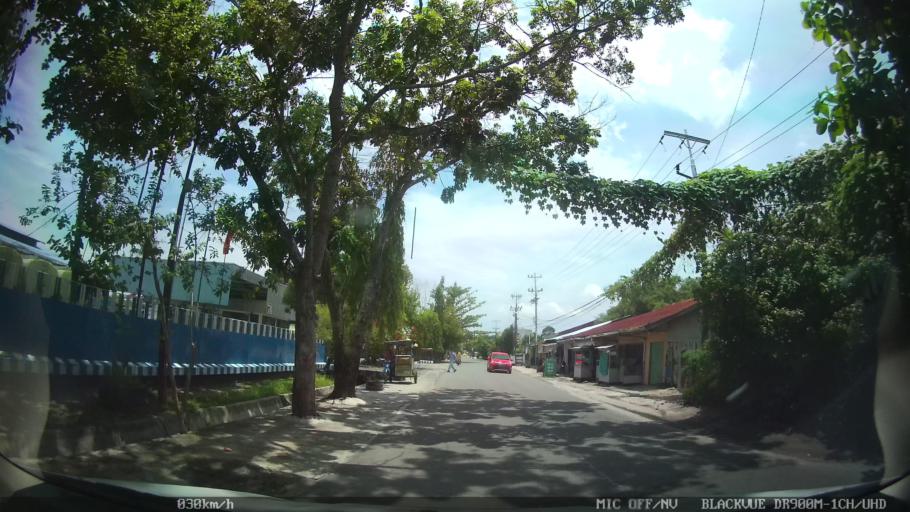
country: ID
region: North Sumatra
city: Percut
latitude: 3.5583
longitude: 98.8625
